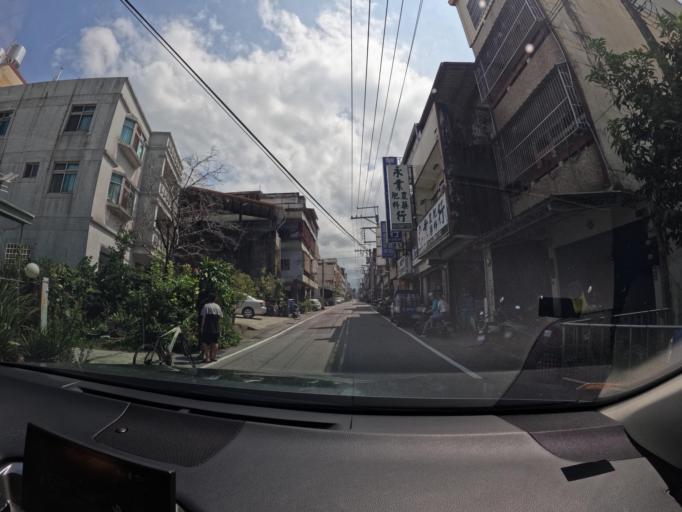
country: TW
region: Taiwan
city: Fengyuan
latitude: 24.3098
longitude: 120.8290
